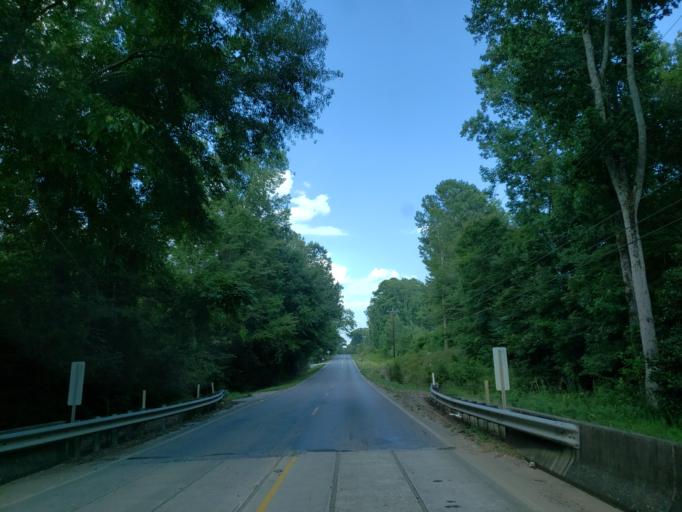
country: US
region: Mississippi
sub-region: Jones County
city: Sharon
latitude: 31.9196
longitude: -89.0283
